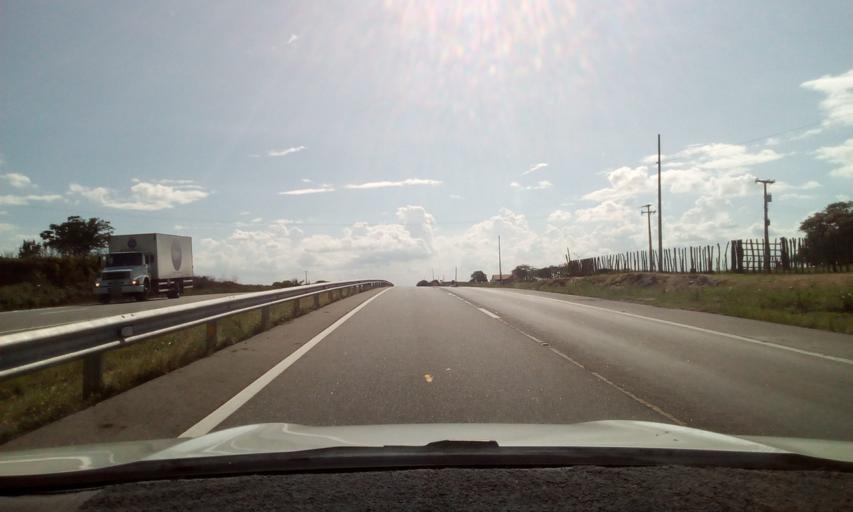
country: BR
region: Paraiba
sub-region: Gurinhem
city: Gurinhem
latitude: -7.1763
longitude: -35.4112
